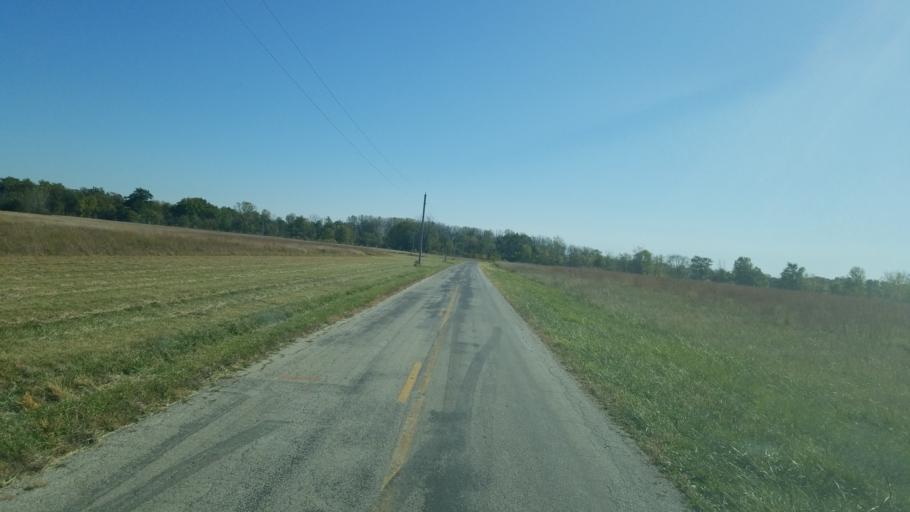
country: US
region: Ohio
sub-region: Union County
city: Richwood
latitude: 40.5611
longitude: -83.3415
